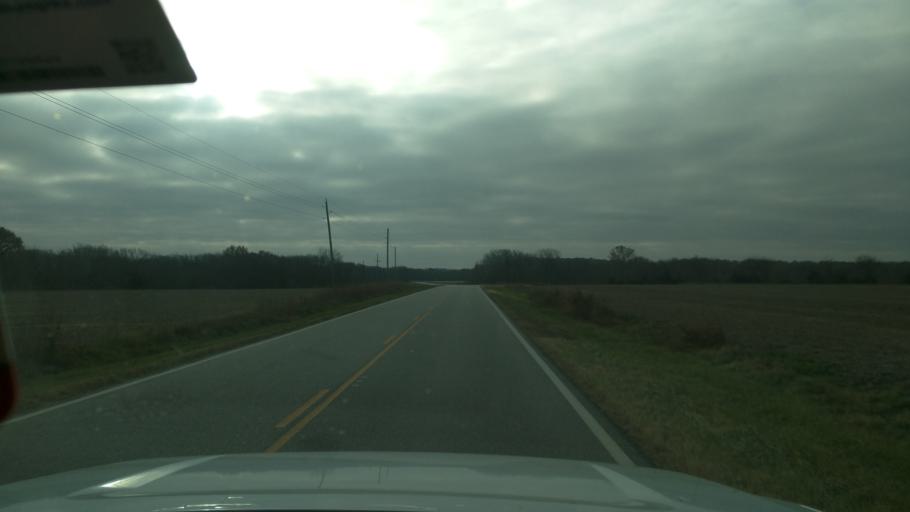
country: US
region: Kansas
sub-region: Greenwood County
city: Eureka
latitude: 37.7133
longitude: -96.2274
